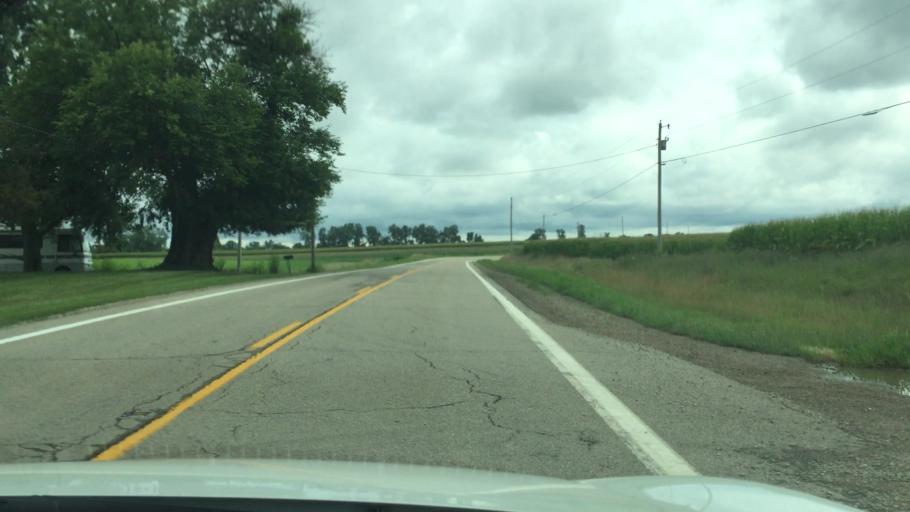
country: US
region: Ohio
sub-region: Champaign County
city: Mechanicsburg
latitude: 40.1194
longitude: -83.5330
